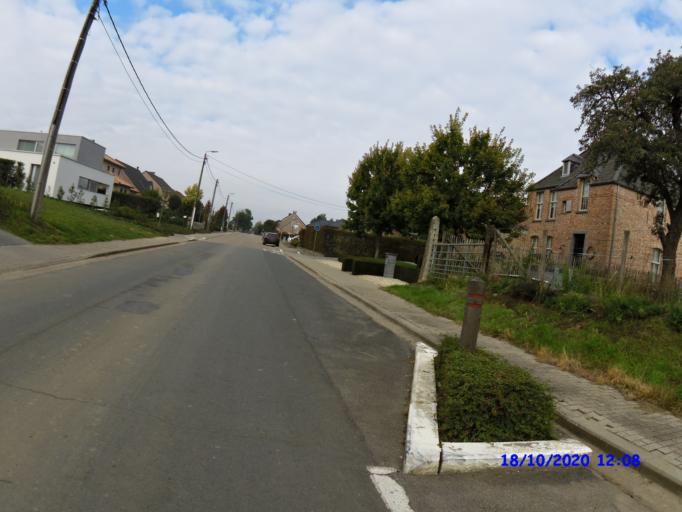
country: BE
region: Flanders
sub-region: Provincie Vlaams-Brabant
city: Landen
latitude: 50.7598
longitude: 5.0748
